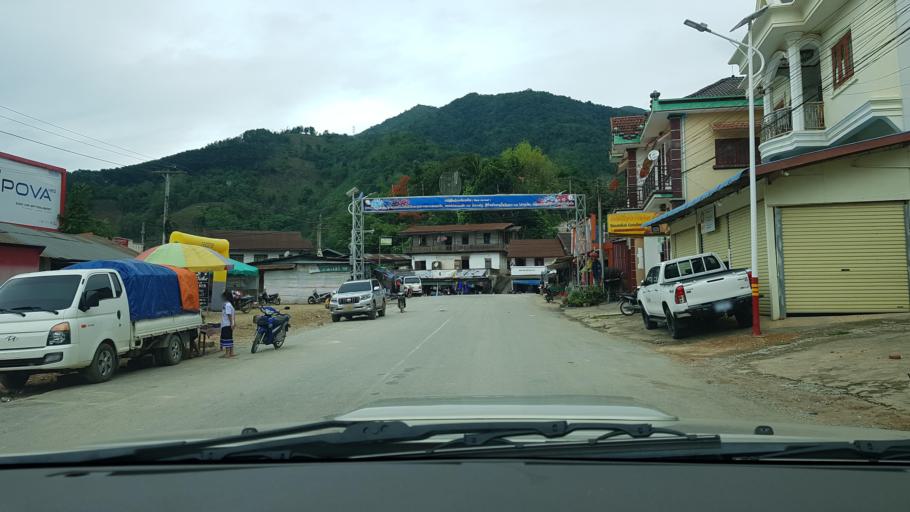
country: LA
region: Phongsali
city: Khoa
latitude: 21.0808
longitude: 102.5063
